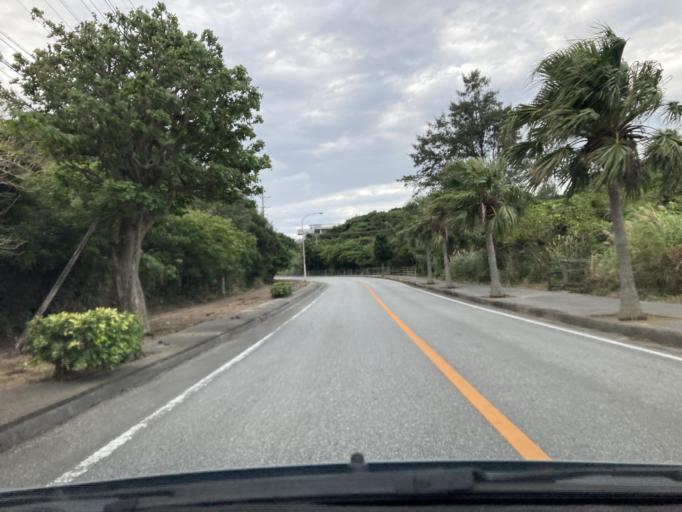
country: JP
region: Okinawa
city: Ishikawa
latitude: 26.4365
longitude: 127.7808
